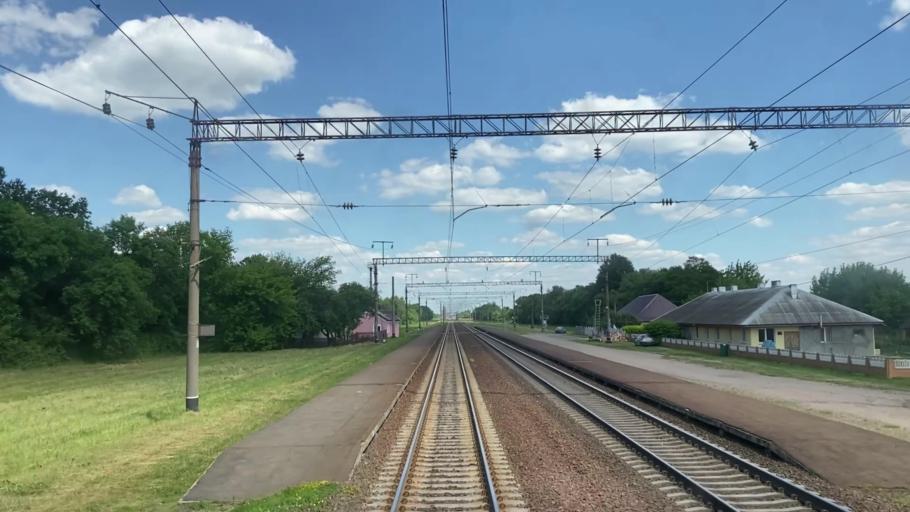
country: BY
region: Brest
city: Charnawchytsy
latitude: 52.1425
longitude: 23.8498
